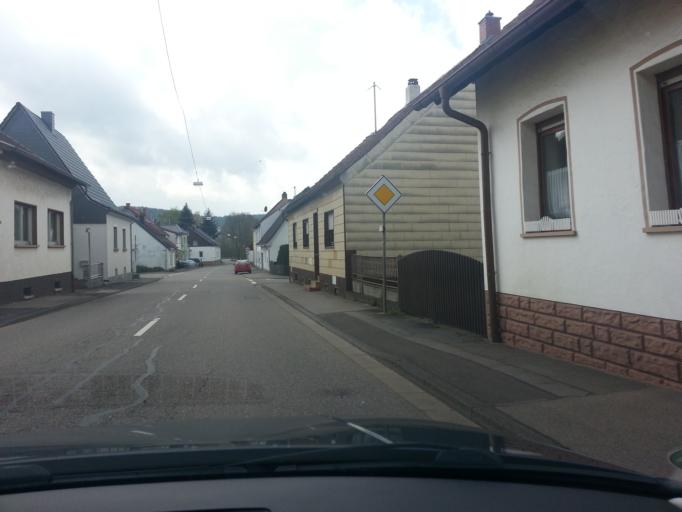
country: DE
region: Saarland
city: Homburg
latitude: 49.3041
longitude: 7.3072
